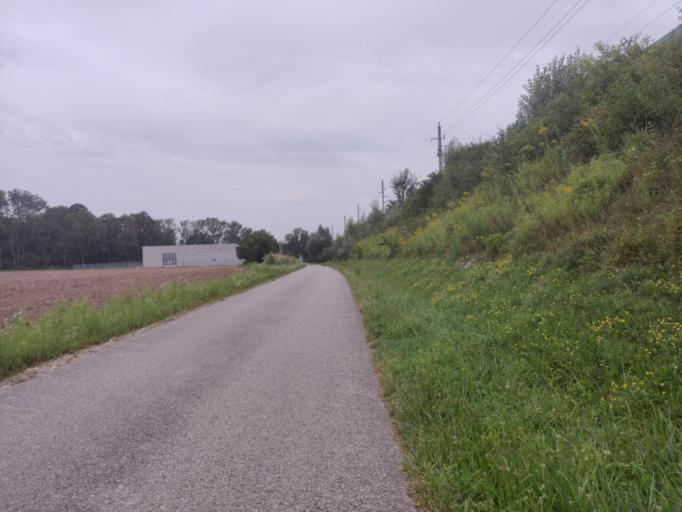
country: AT
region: Lower Austria
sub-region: Politischer Bezirk Amstetten
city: Ennsdorf
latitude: 48.2218
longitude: 14.4958
